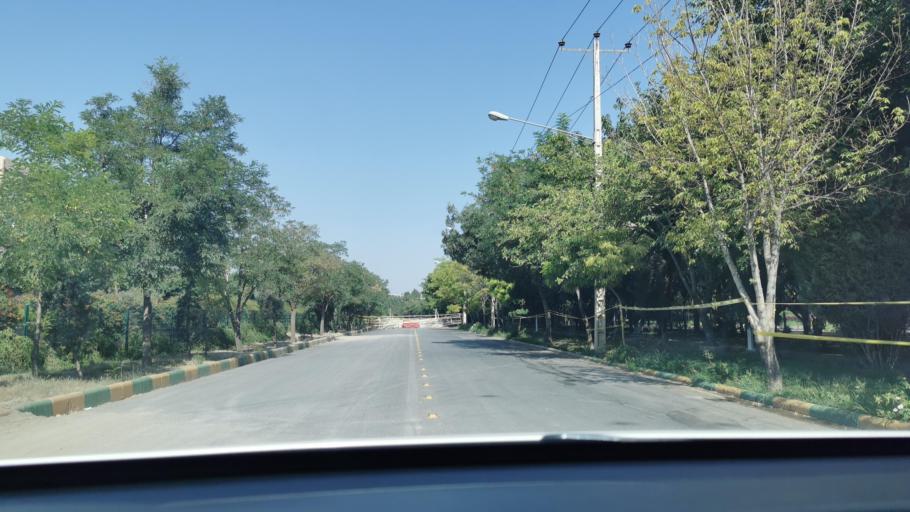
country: IR
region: Razavi Khorasan
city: Mashhad
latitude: 36.3305
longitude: 59.6327
